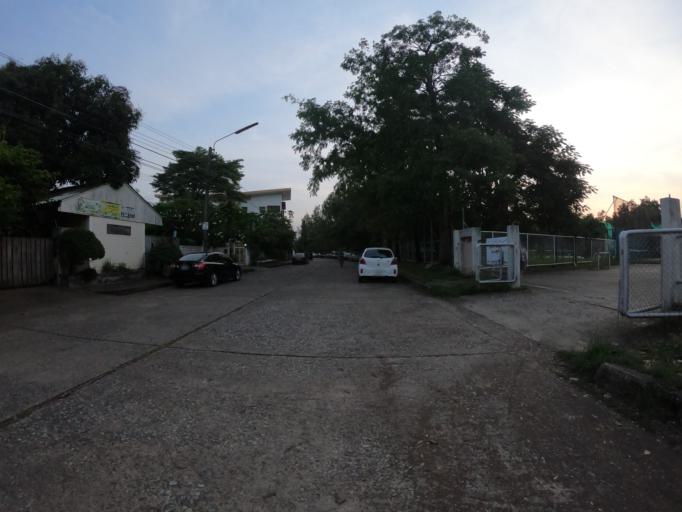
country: TH
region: Bangkok
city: Lat Phrao
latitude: 13.8289
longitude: 100.6101
